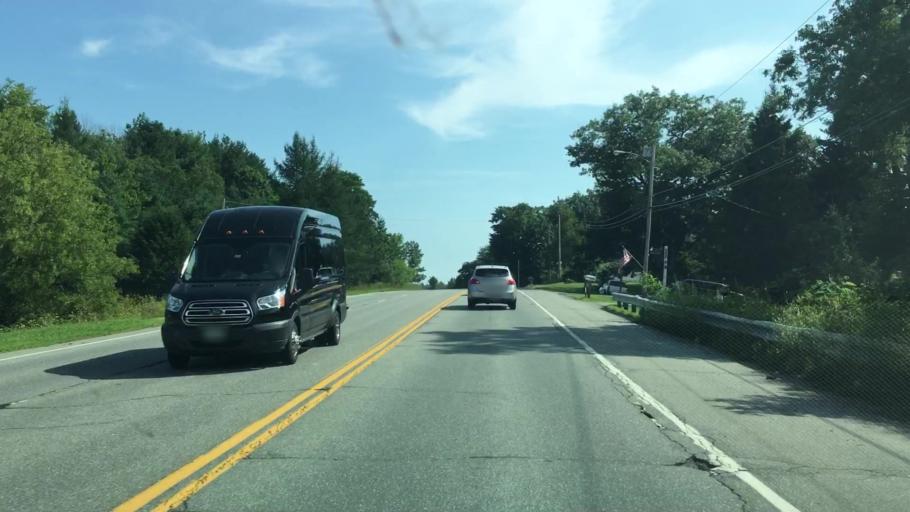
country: US
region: Maine
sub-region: Penobscot County
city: Orrington
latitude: 44.7092
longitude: -68.8472
